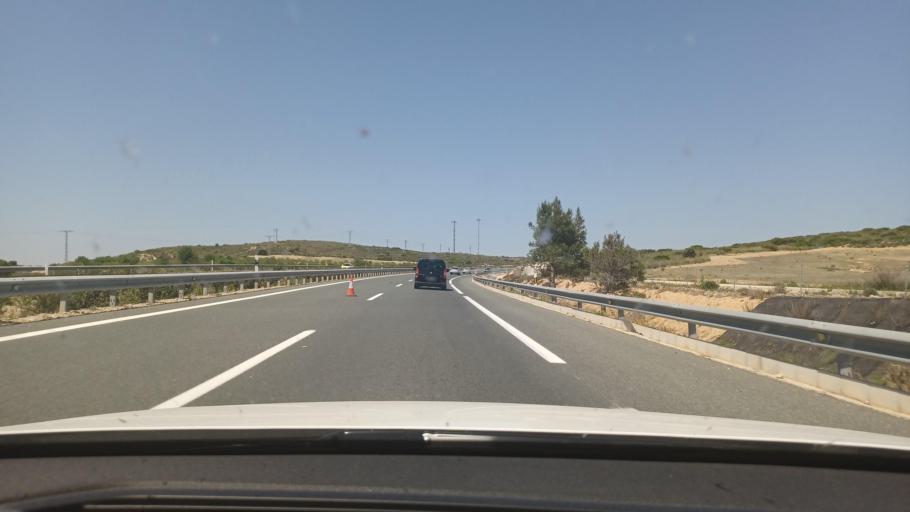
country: ES
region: Castille-La Mancha
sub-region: Provincia de Albacete
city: Alpera
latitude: 38.8780
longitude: -1.1927
